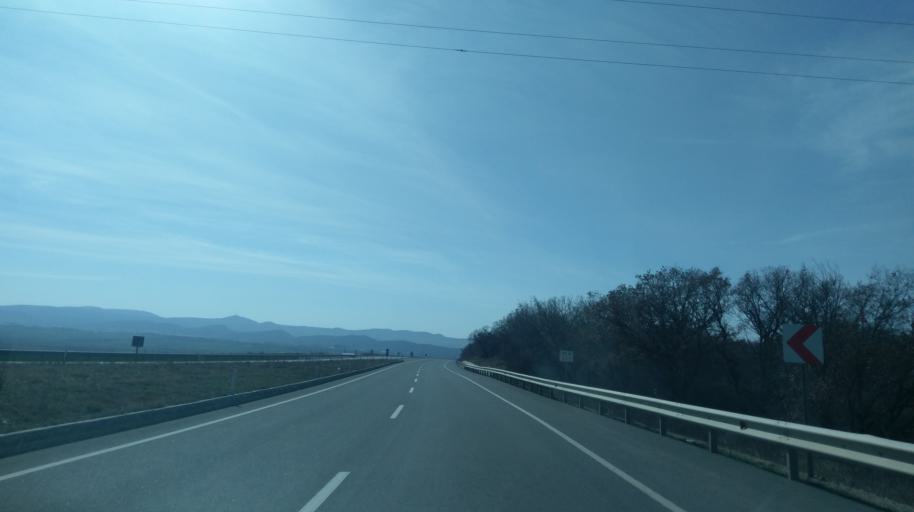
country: TR
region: Edirne
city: Kesan
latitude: 40.9045
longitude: 26.6320
